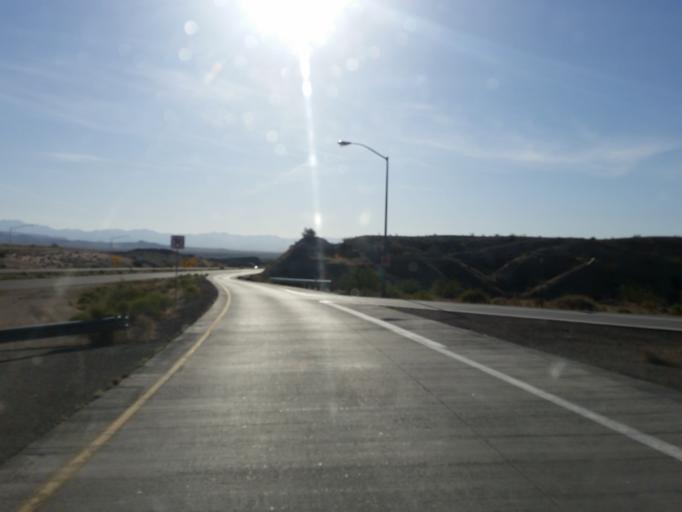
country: US
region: Arizona
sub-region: Mohave County
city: Desert Hills
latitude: 34.7235
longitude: -114.4189
